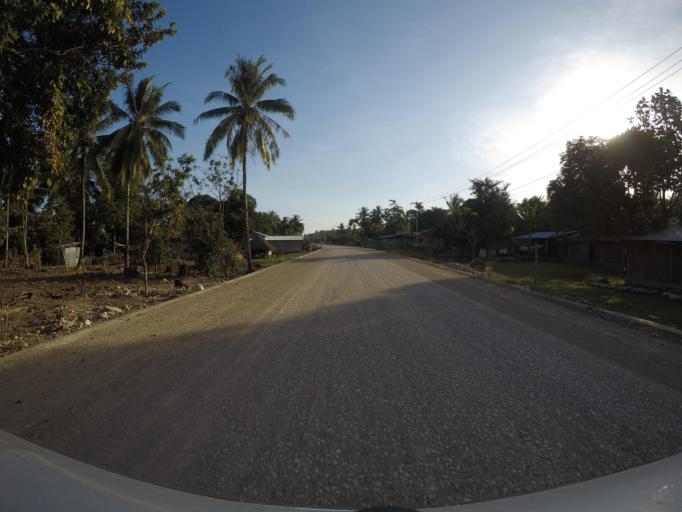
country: TL
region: Viqueque
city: Viqueque
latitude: -8.8100
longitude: 126.5399
